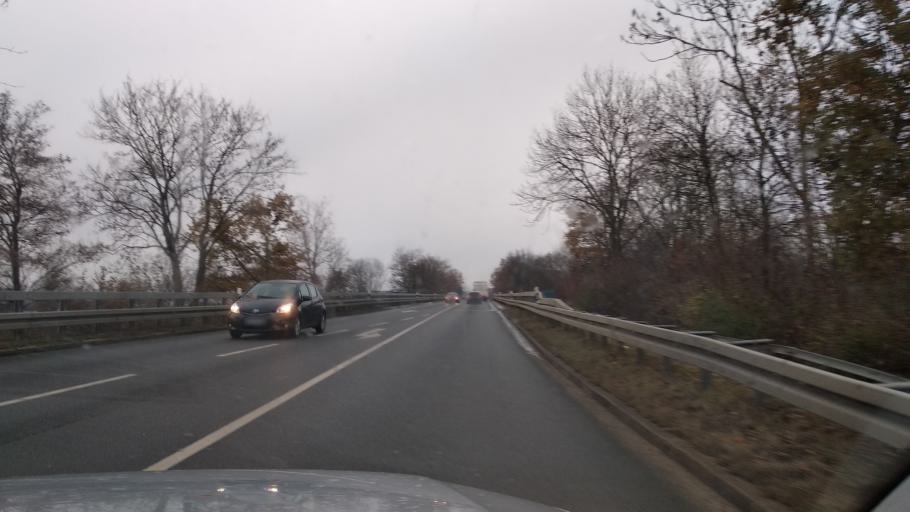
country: DE
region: Bavaria
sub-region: Upper Bavaria
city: Feldkirchen
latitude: 48.1528
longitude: 11.7543
